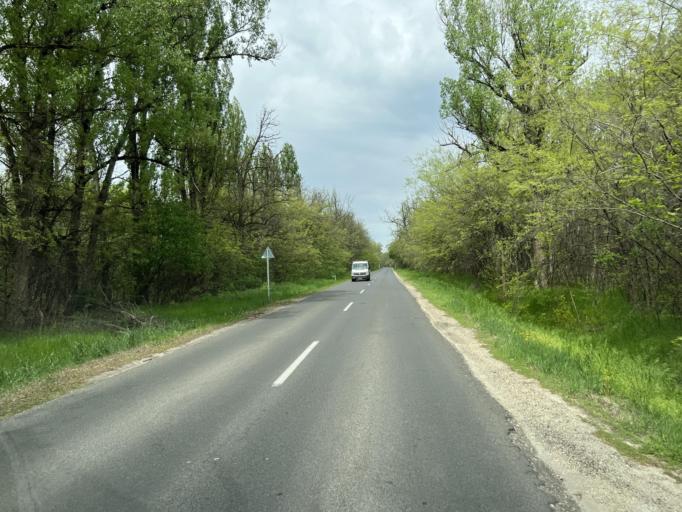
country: HU
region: Pest
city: Tortel
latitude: 47.1468
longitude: 19.8682
